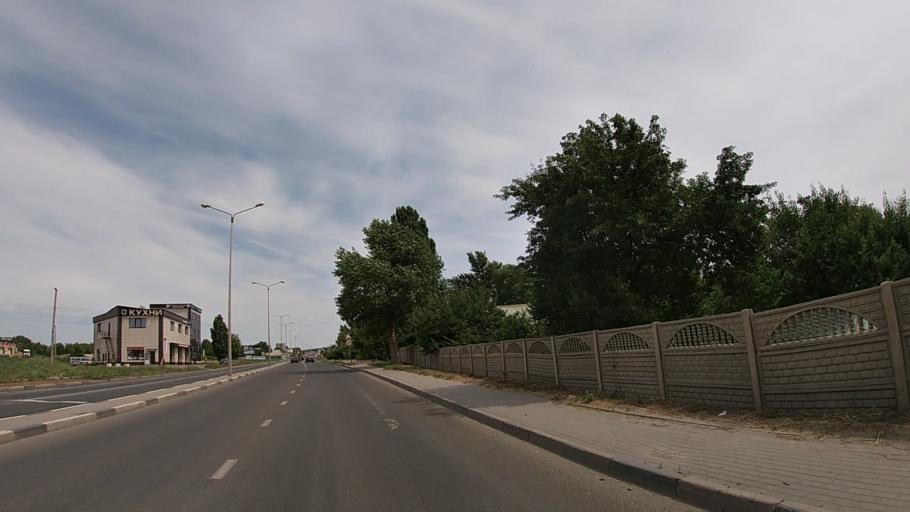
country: RU
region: Belgorod
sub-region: Belgorodskiy Rayon
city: Belgorod
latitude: 50.6175
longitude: 36.5390
